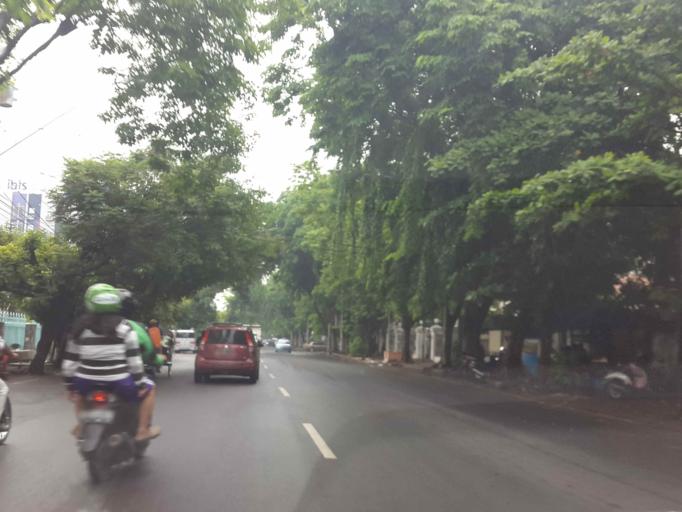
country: ID
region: Central Java
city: Semarang
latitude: -6.9786
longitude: 110.4121
